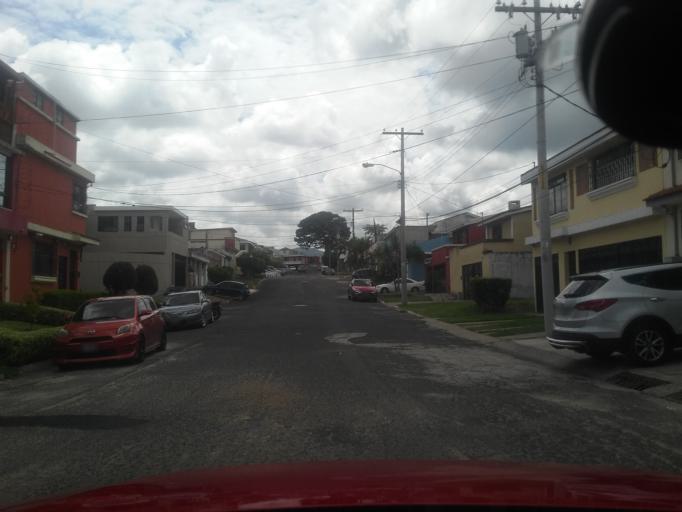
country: GT
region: Guatemala
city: Mixco
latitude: 14.6454
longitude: -90.5653
